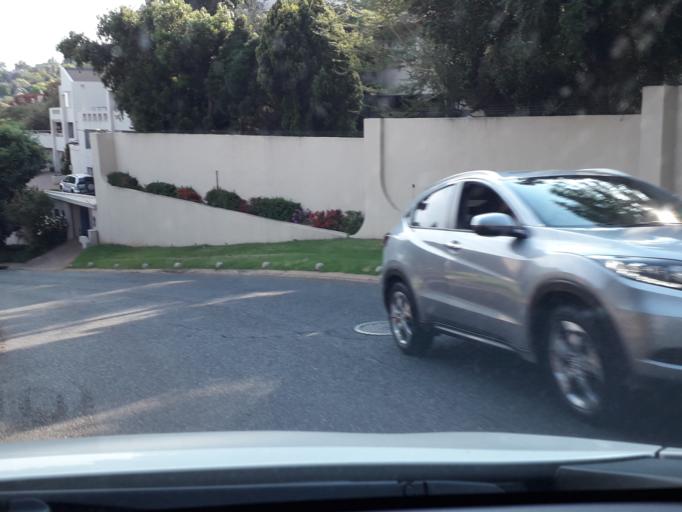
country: ZA
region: Gauteng
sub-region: City of Johannesburg Metropolitan Municipality
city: Roodepoort
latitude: -26.1514
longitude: 27.9592
